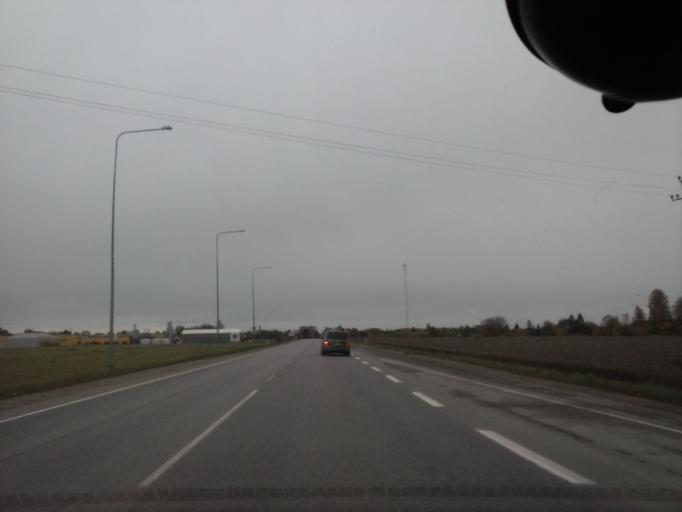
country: EE
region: Jogevamaa
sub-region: Poltsamaa linn
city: Poltsamaa
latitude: 58.7442
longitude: 25.7692
